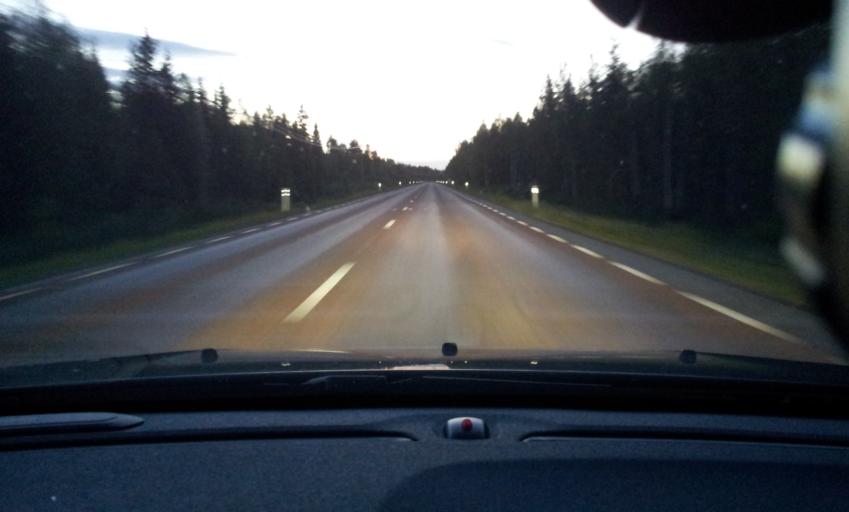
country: SE
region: Jaemtland
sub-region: Bergs Kommun
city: Hoverberg
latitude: 62.8554
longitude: 14.5180
